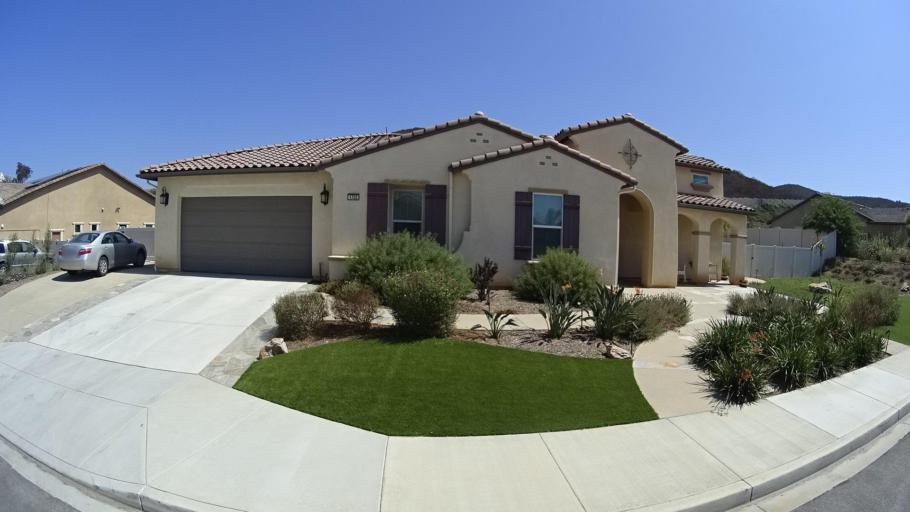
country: US
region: California
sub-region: San Diego County
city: San Marcos
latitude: 33.1835
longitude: -117.1937
